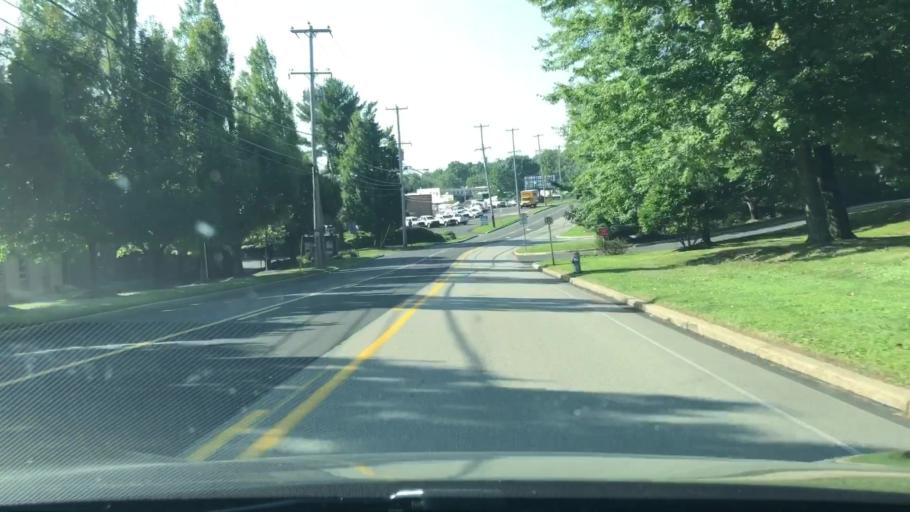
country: US
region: Pennsylvania
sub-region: Montgomery County
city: Horsham
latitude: 40.1581
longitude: -75.1358
